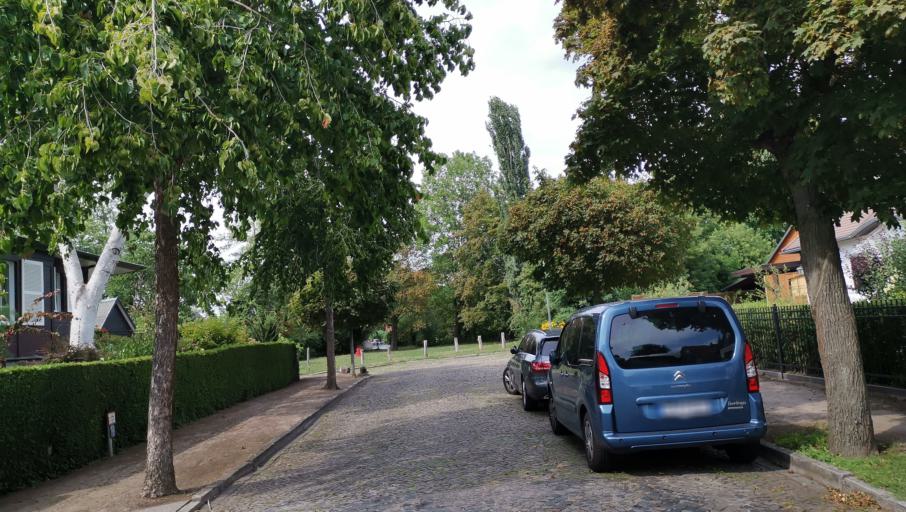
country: DE
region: Brandenburg
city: Potsdam
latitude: 52.3899
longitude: 13.0491
